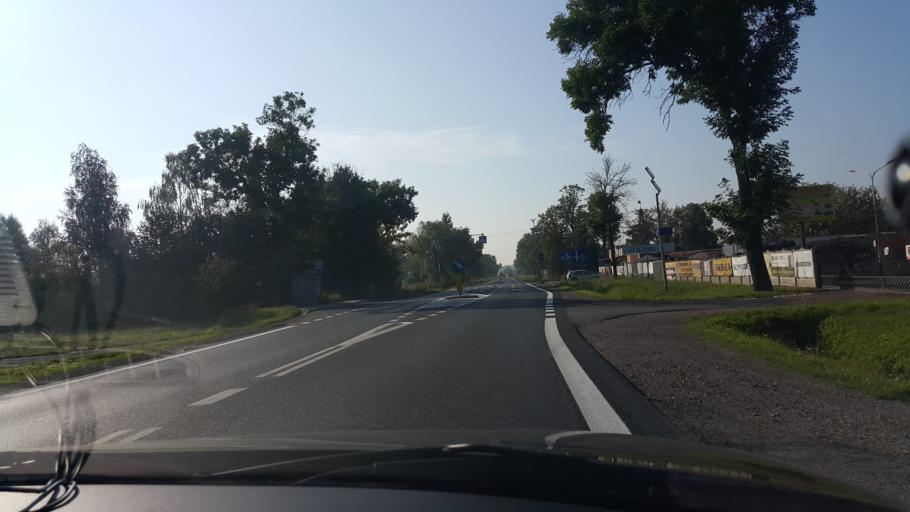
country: PL
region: Masovian Voivodeship
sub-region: Powiat radomski
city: Jedlnia-Letnisko
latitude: 51.3935
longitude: 21.2685
